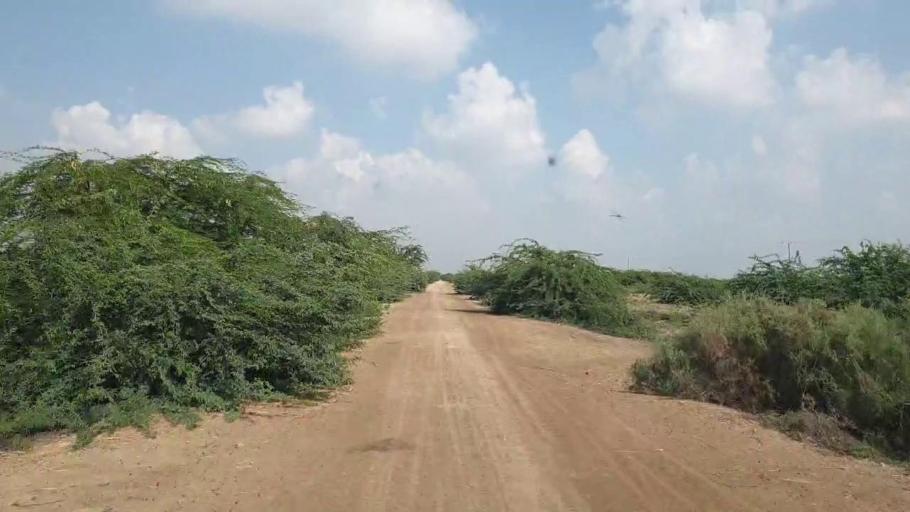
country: PK
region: Sindh
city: Badin
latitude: 24.4907
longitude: 68.6532
